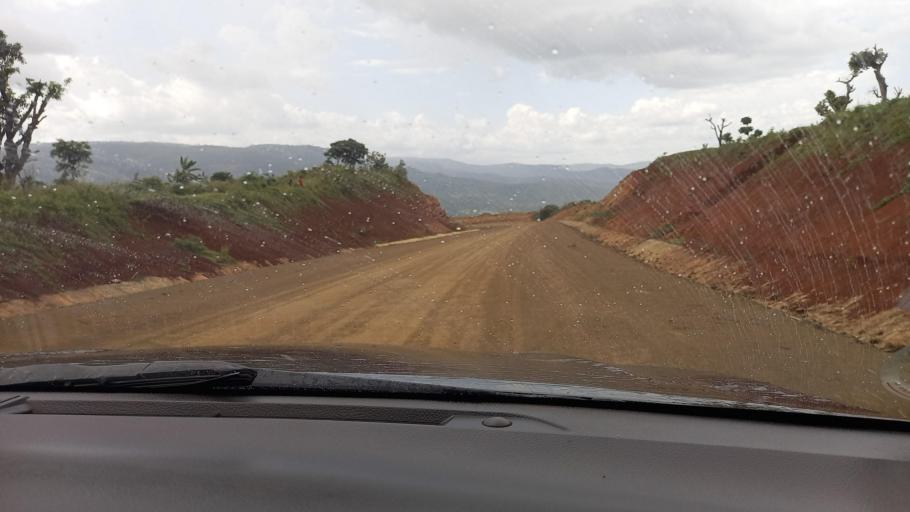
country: ET
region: Southern Nations, Nationalities, and People's Region
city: Mizan Teferi
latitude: 6.1803
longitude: 35.7005
